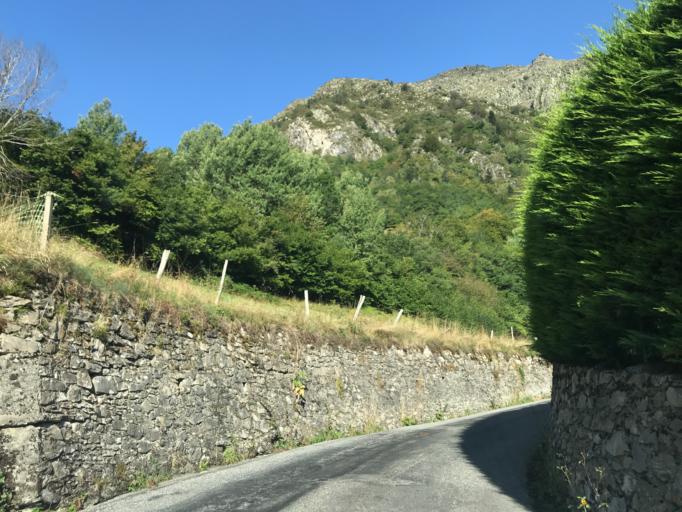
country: FR
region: Midi-Pyrenees
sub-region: Departement des Hautes-Pyrenees
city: Saint-Lary-Soulan
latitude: 42.7909
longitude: 0.2273
